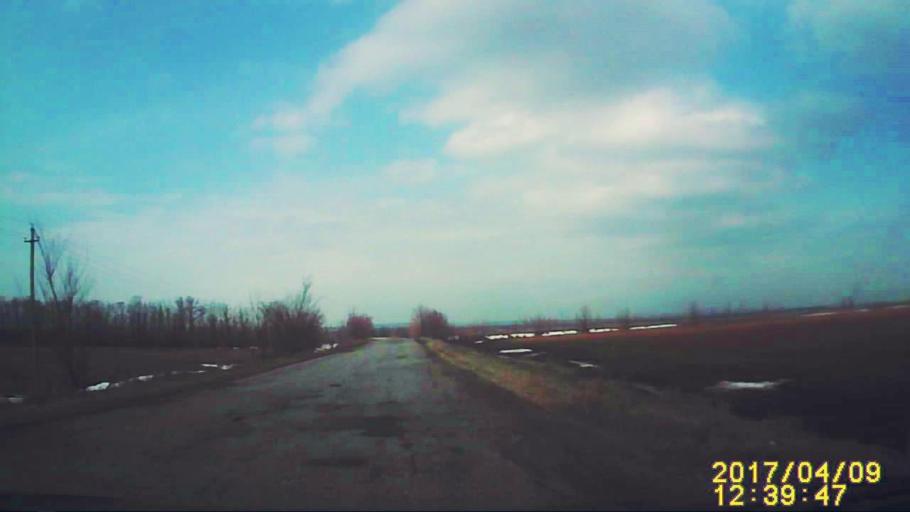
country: RU
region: Ulyanovsk
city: Ignatovka
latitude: 54.0005
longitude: 47.9527
